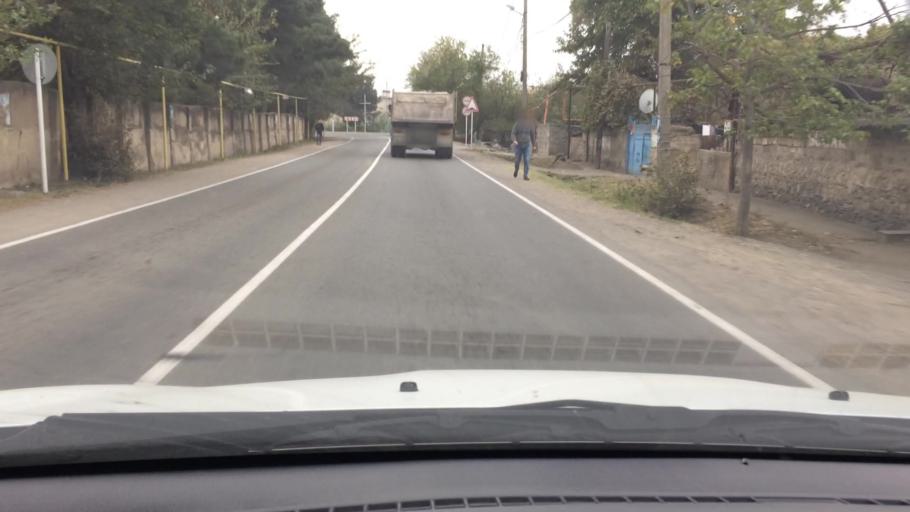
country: GE
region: Kvemo Kartli
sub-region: Marneuli
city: Marneuli
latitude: 41.4784
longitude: 44.7988
